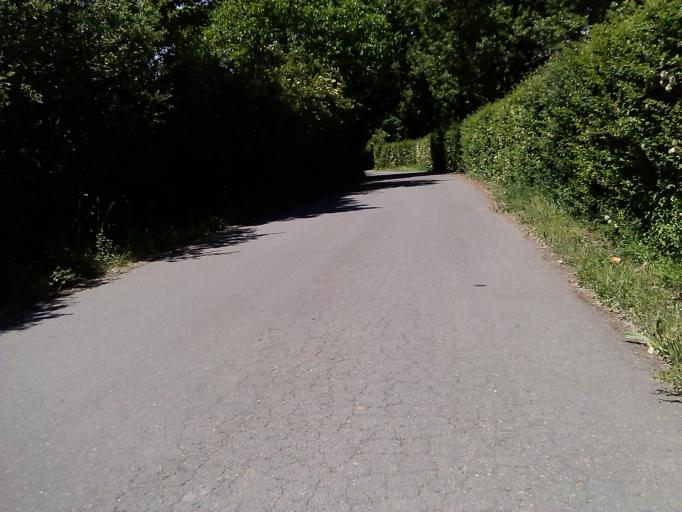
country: ES
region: Castille and Leon
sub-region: Provincia de Leon
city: Leon
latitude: 42.5948
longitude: -5.5505
